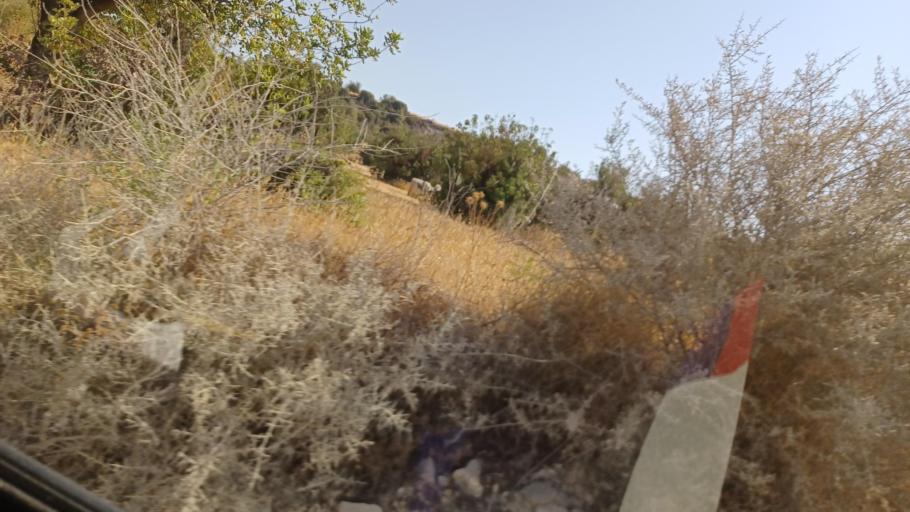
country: CY
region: Limassol
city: Pissouri
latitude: 34.7122
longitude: 32.6762
